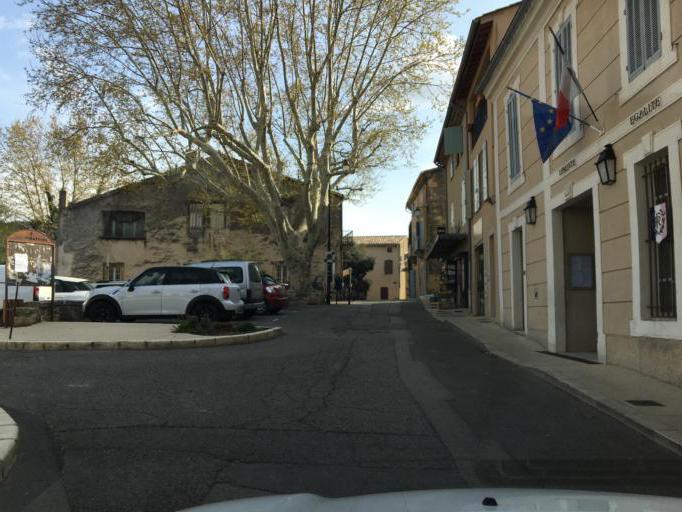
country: FR
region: Provence-Alpes-Cote d'Azur
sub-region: Departement du Vaucluse
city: Ansouis
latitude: 43.7381
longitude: 5.4650
